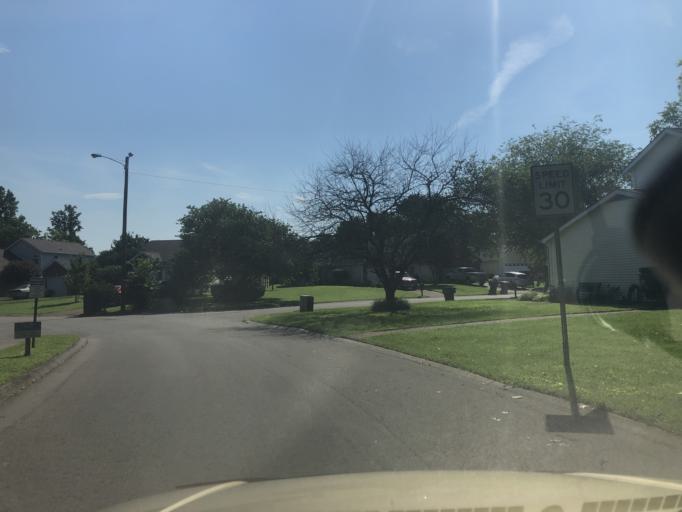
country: US
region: Tennessee
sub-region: Davidson County
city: Lakewood
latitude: 36.2349
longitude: -86.6991
